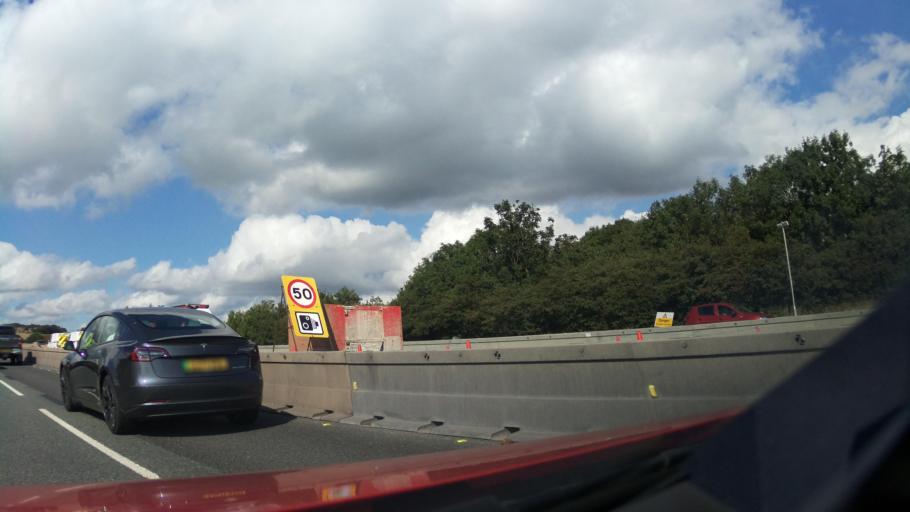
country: GB
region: England
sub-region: Borough of Wigan
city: Ashton in Makerfield
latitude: 53.5095
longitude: -2.6732
